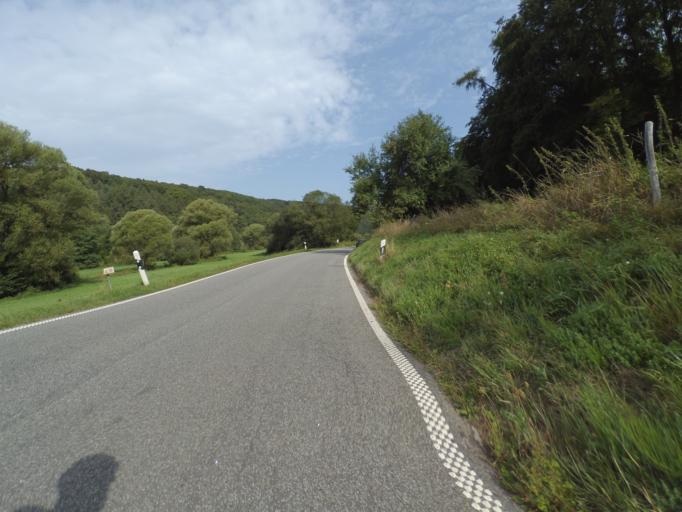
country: DE
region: Rheinland-Pfalz
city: Tawern
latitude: 49.6537
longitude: 6.5095
